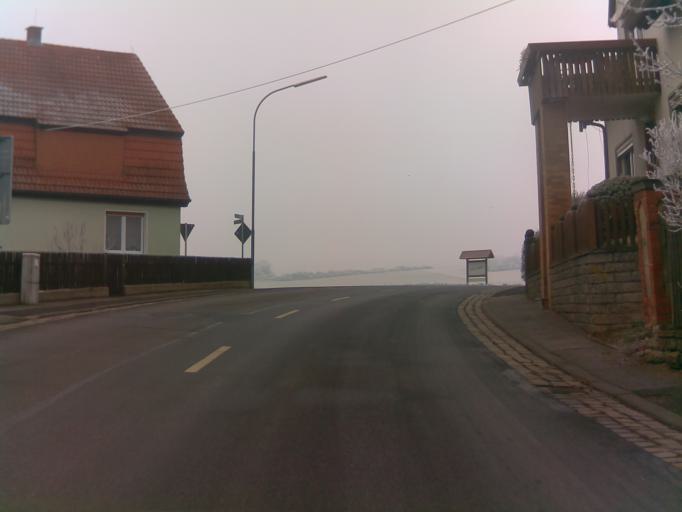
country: DE
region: Bavaria
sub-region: Regierungsbezirk Unterfranken
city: Sondheim vor der Rhoen
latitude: 50.4632
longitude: 10.1573
